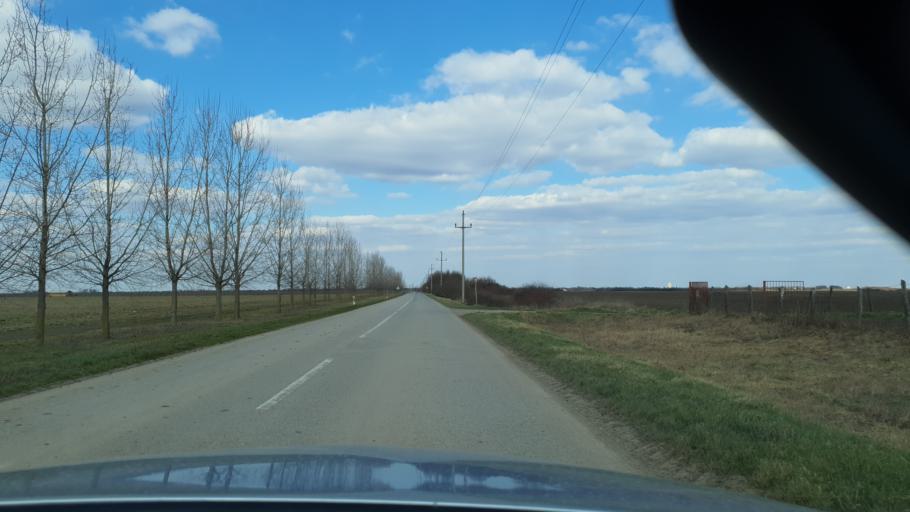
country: RS
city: Kulpin
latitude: 45.4231
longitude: 19.6004
